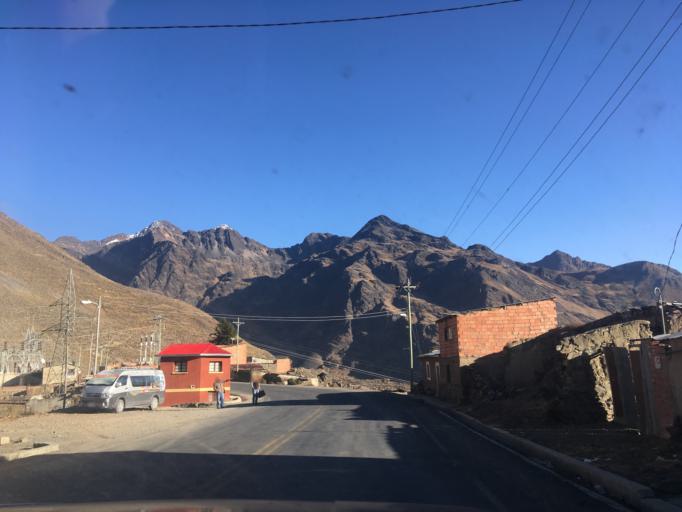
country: BO
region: La Paz
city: Quime
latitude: -17.0335
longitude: -67.2830
